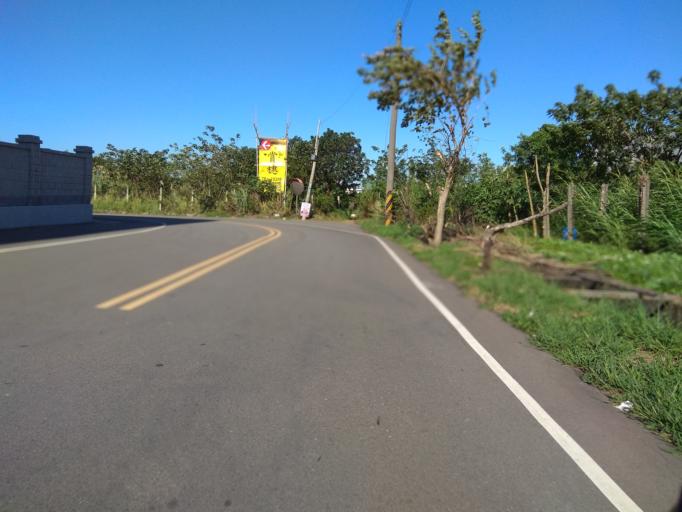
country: TW
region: Taiwan
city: Taoyuan City
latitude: 24.9680
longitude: 121.1525
